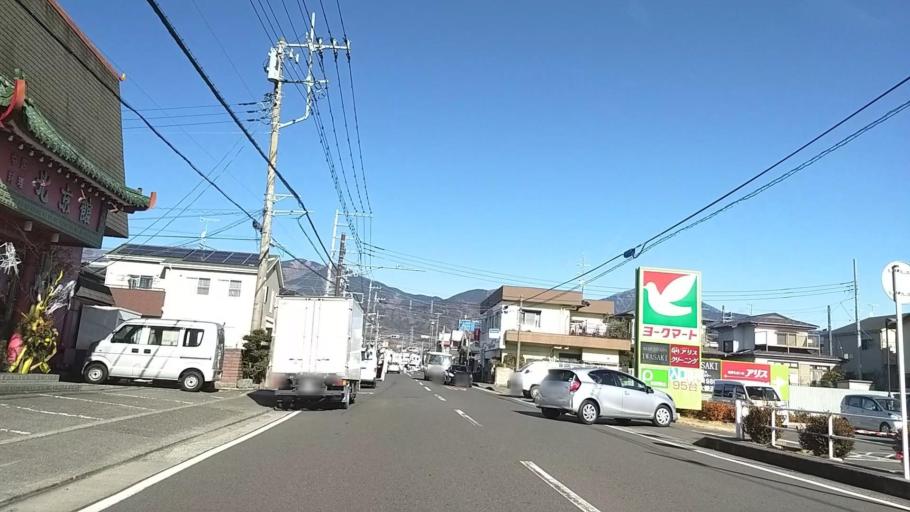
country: JP
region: Kanagawa
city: Hadano
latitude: 35.3745
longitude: 139.2082
